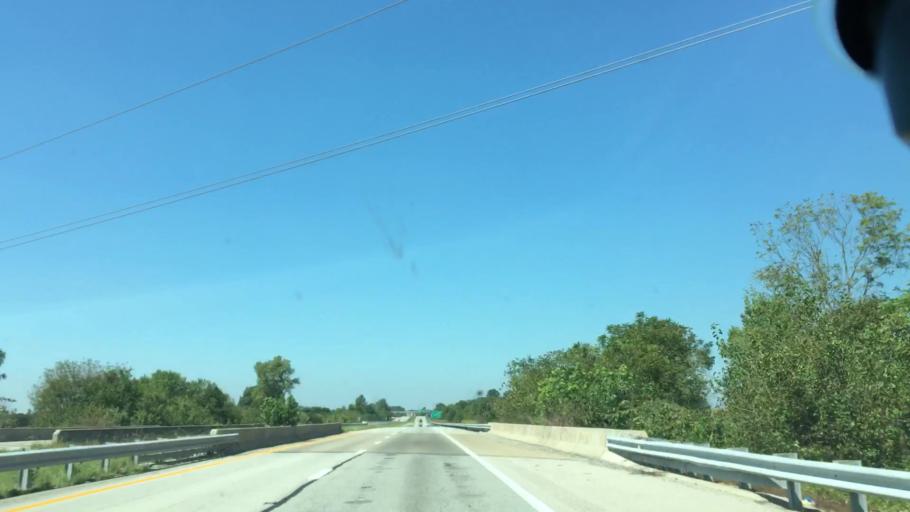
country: US
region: Kentucky
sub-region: Henderson County
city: Henderson
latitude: 37.7861
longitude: -87.5490
